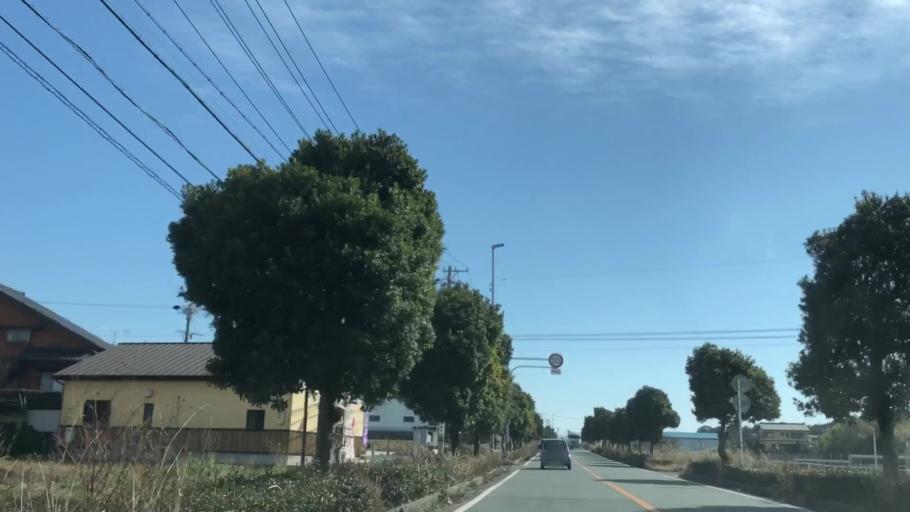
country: JP
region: Aichi
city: Toyohashi
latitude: 34.7053
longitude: 137.4120
